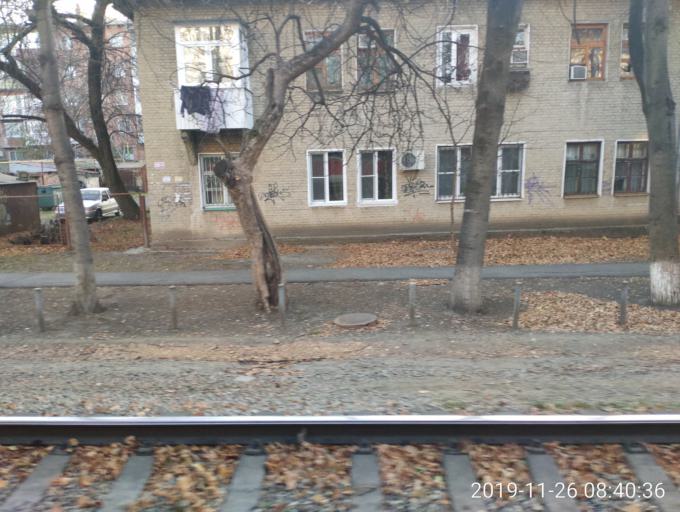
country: RU
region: Krasnodarskiy
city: Krasnodar
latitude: 45.0550
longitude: 38.9841
